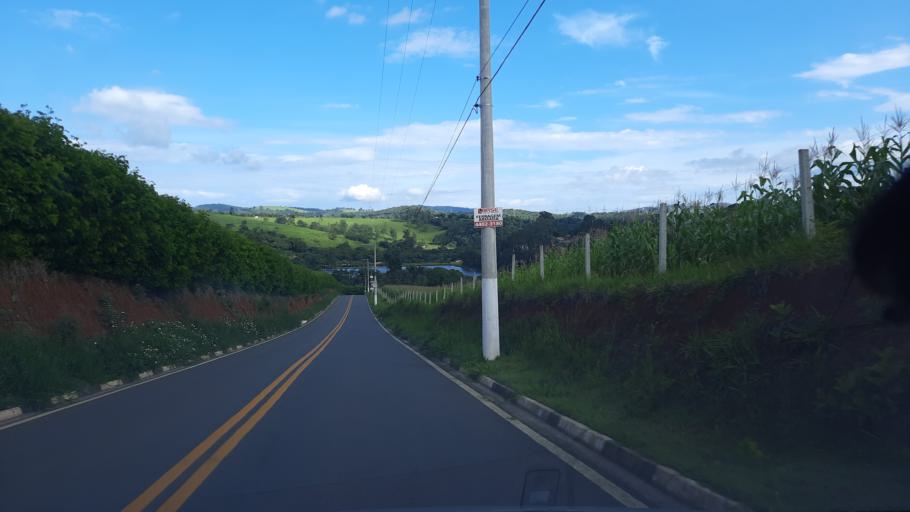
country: BR
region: Sao Paulo
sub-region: Atibaia
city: Atibaia
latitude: -23.0837
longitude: -46.5079
